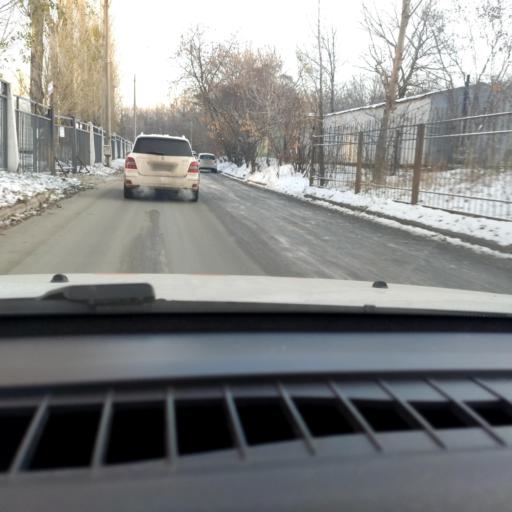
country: RU
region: Samara
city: Tol'yatti
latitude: 53.5006
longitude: 49.3016
